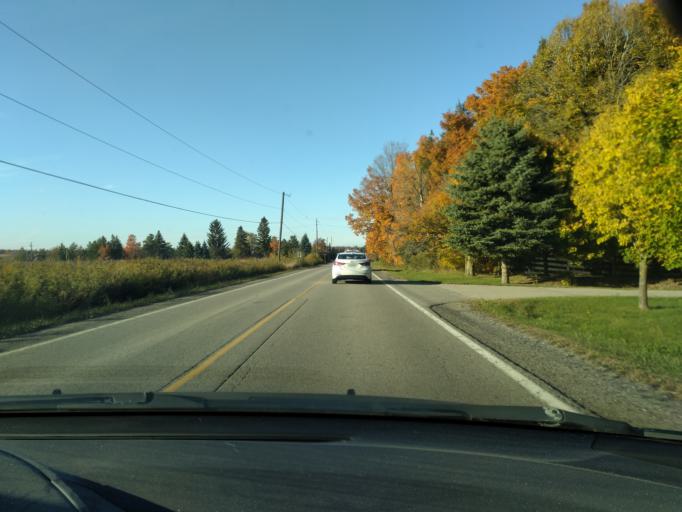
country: CA
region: Ontario
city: Bradford West Gwillimbury
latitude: 43.9806
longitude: -79.7228
